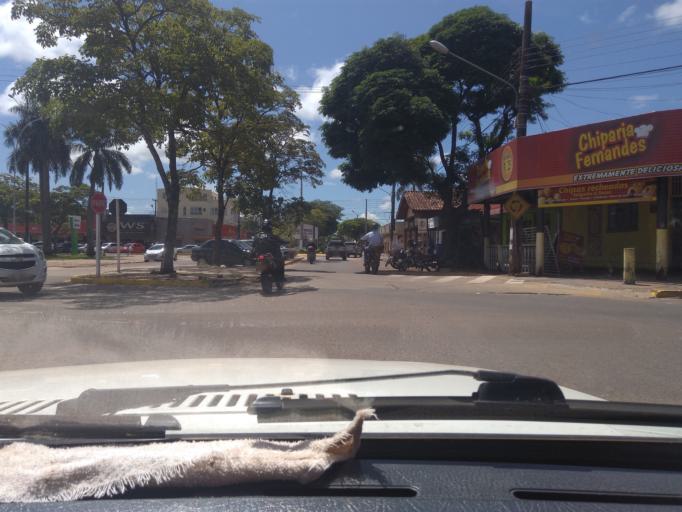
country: BR
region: Mato Grosso do Sul
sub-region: Ponta Pora
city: Ponta Pora
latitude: -22.5389
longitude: -55.7306
